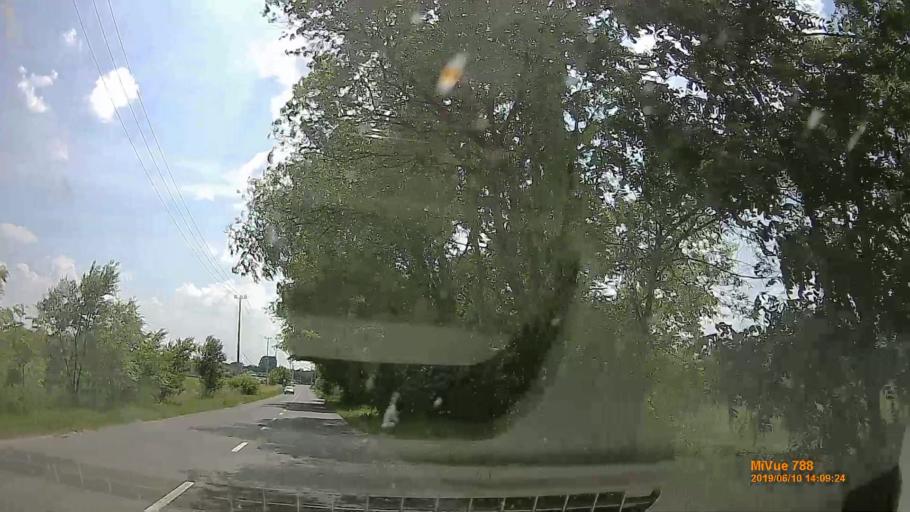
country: HU
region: Pest
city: God
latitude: 47.6818
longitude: 19.1516
